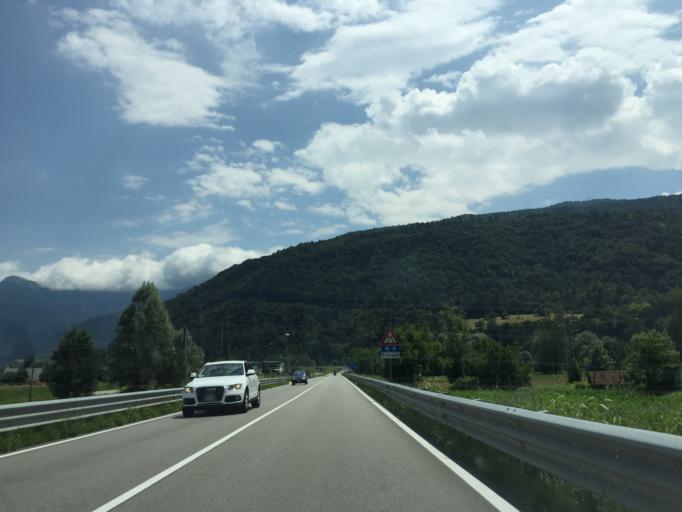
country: IT
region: Veneto
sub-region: Provincia di Belluno
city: Fonzaso
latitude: 46.0054
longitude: 11.8024
